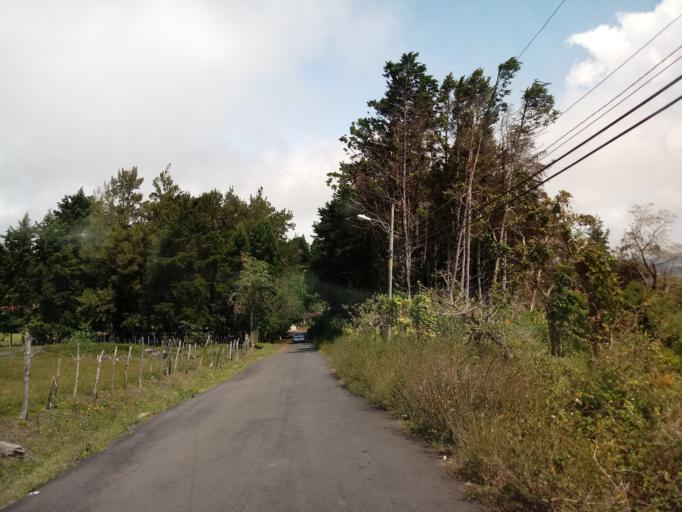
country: CR
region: Heredia
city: Angeles
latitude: 10.0359
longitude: -84.0388
